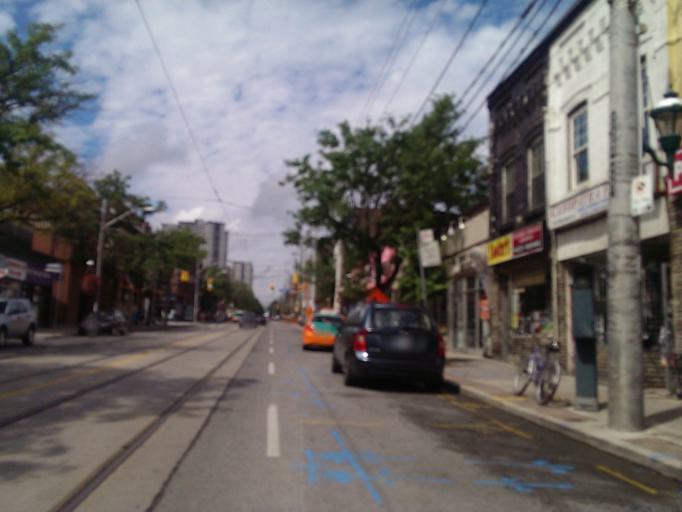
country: CA
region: Ontario
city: Toronto
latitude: 43.6634
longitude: -79.3675
